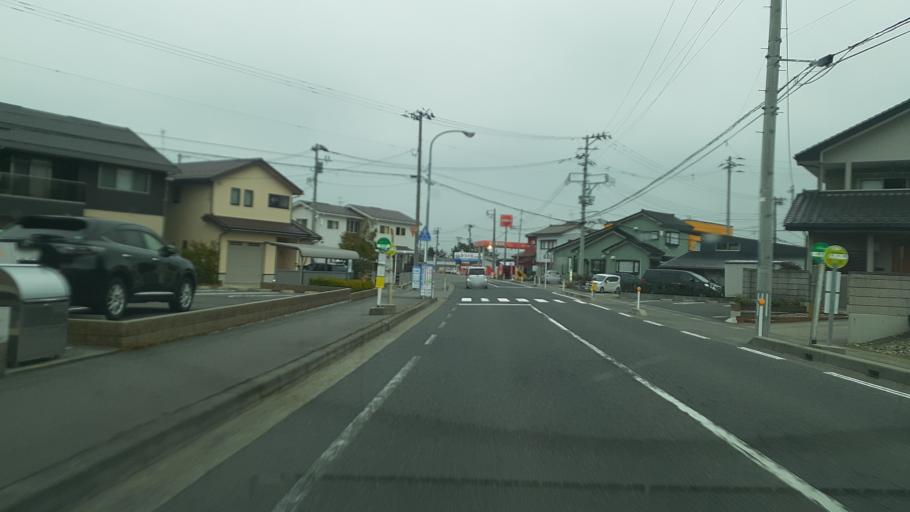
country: JP
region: Niigata
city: Niigata-shi
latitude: 37.8545
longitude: 139.0370
